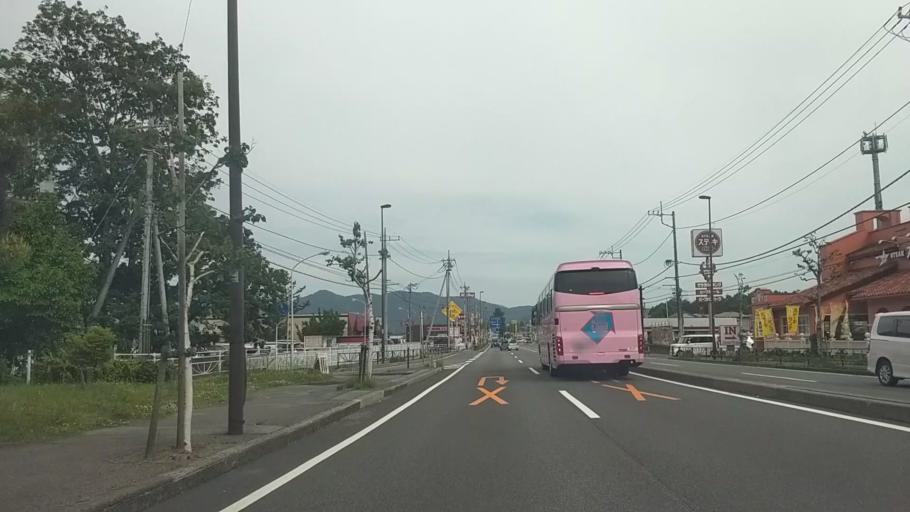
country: JP
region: Yamanashi
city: Fujikawaguchiko
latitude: 35.4833
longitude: 138.7783
